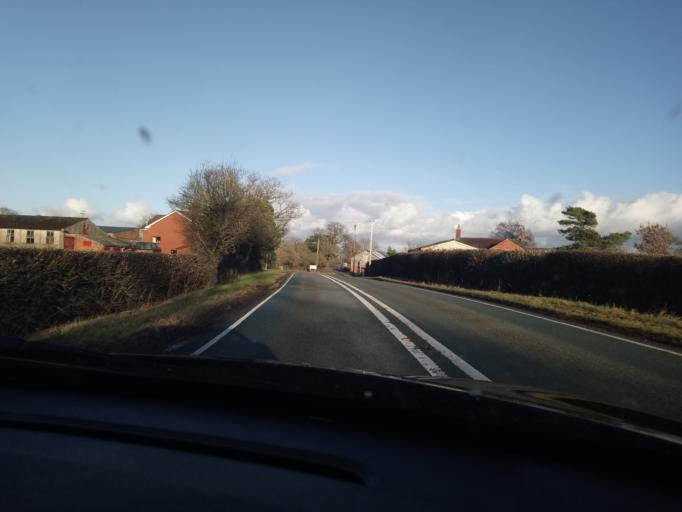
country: GB
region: Wales
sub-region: Wrexham
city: Overton
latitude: 52.9263
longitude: -2.9594
